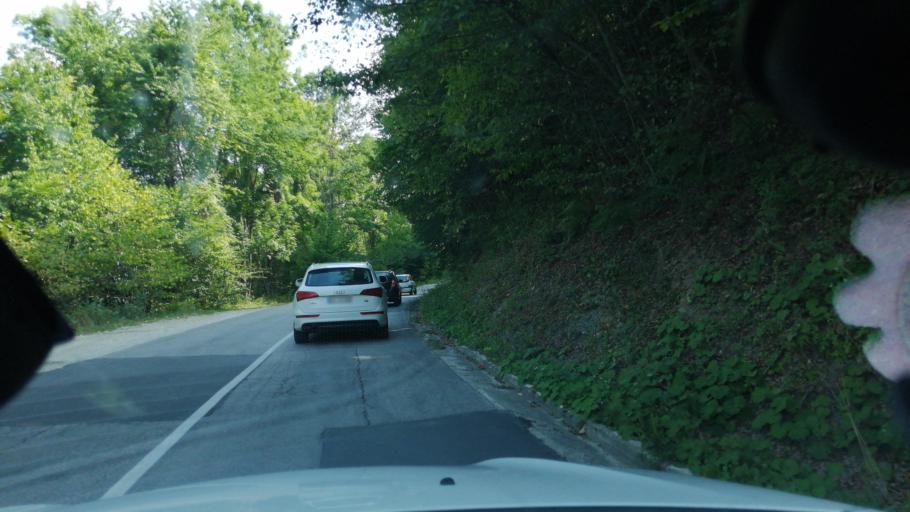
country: RS
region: Central Serbia
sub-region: Moravicki Okrug
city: Ivanjica
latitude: 43.6697
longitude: 20.2653
